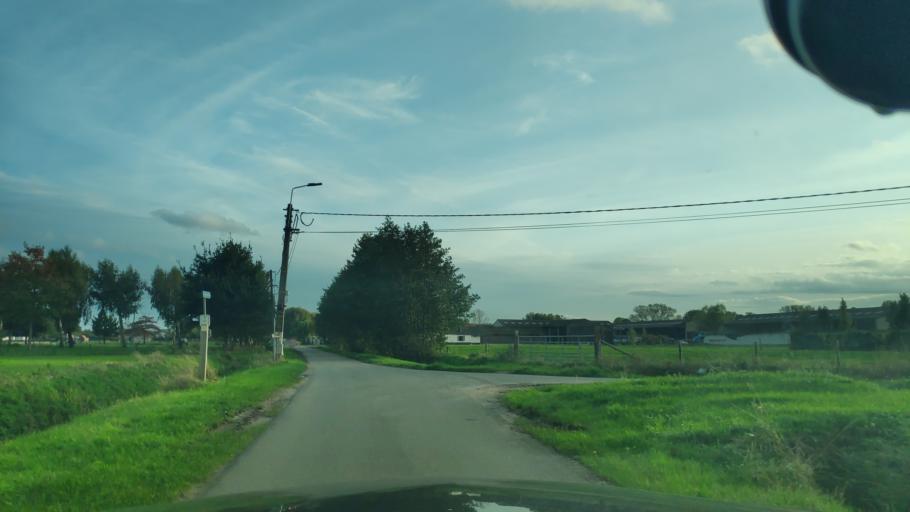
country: BE
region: Flanders
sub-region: Provincie Oost-Vlaanderen
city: Aalter
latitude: 51.1220
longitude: 3.4431
